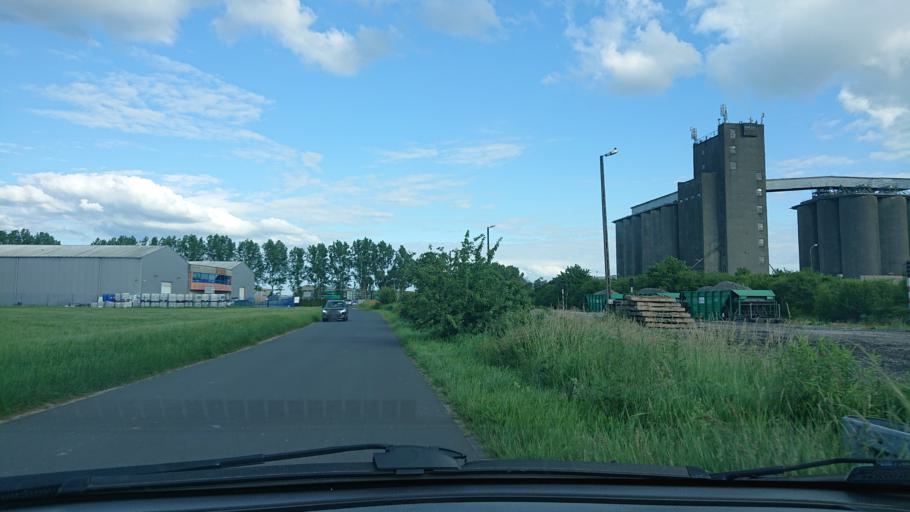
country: PL
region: Greater Poland Voivodeship
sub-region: Powiat gnieznienski
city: Gniezno
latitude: 52.5577
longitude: 17.6151
